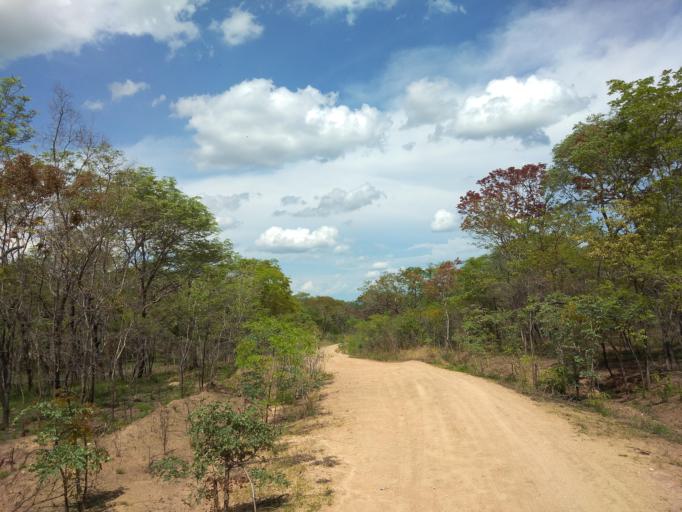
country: ZM
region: Eastern
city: Nyimba
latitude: -14.1260
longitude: 30.0859
